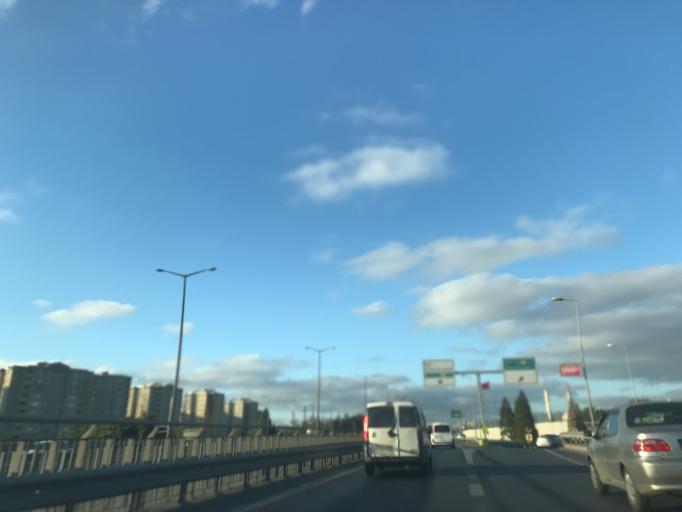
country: TR
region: Istanbul
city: Esenler
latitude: 41.0454
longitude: 28.8849
